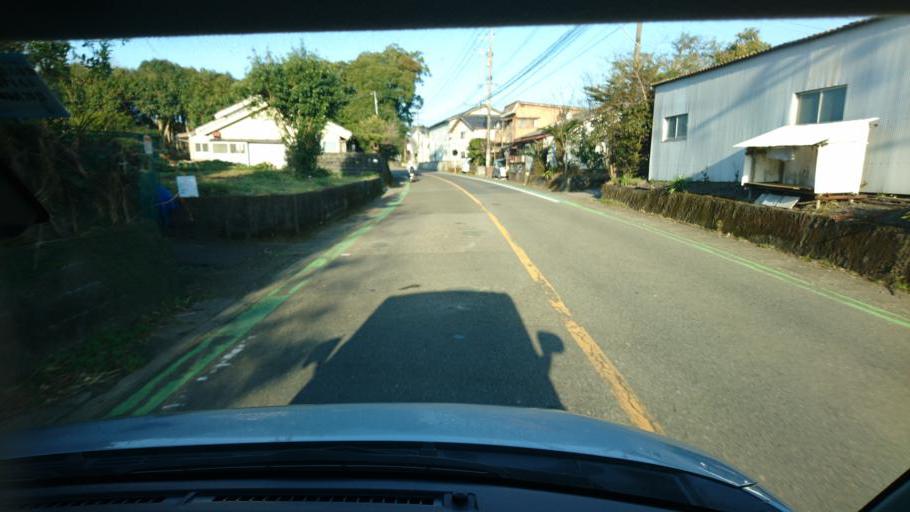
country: JP
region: Miyazaki
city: Miyazaki-shi
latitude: 31.8422
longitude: 131.4154
